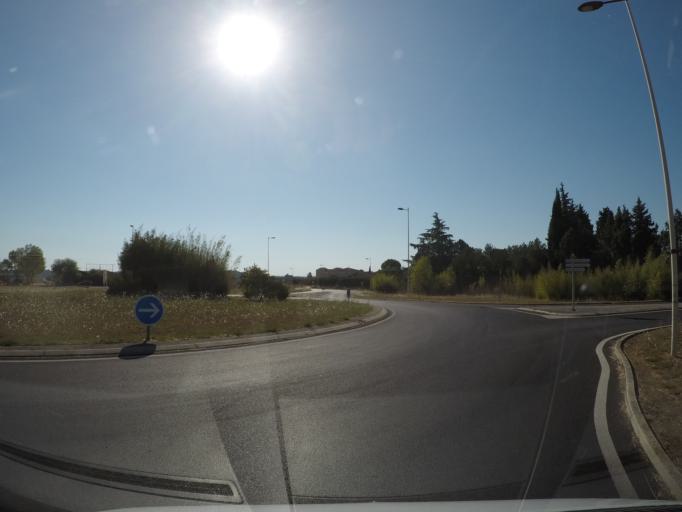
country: FR
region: Languedoc-Roussillon
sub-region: Departement du Gard
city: Lezan
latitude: 44.0246
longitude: 4.0253
